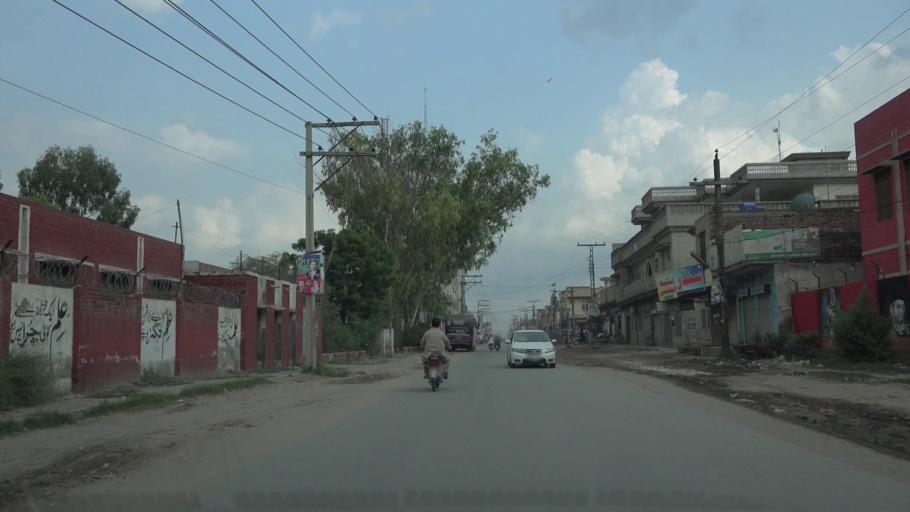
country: PK
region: Punjab
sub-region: Nankana Sahib District
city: Shahkot
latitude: 31.5725
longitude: 73.4858
